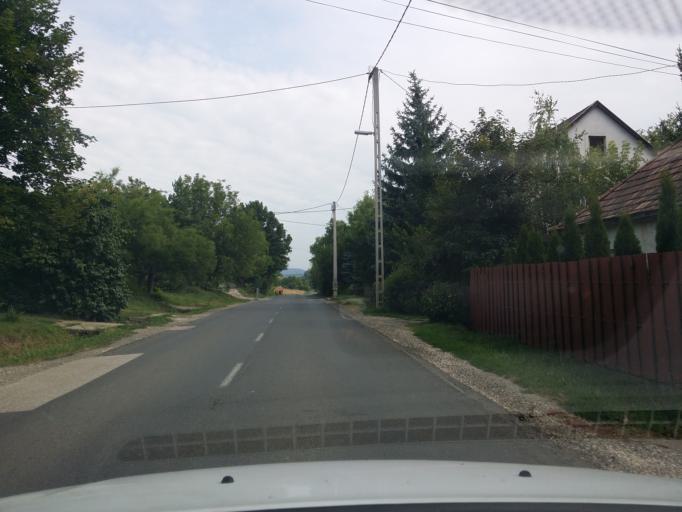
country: HU
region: Pest
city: Acsa
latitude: 47.8025
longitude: 19.3854
